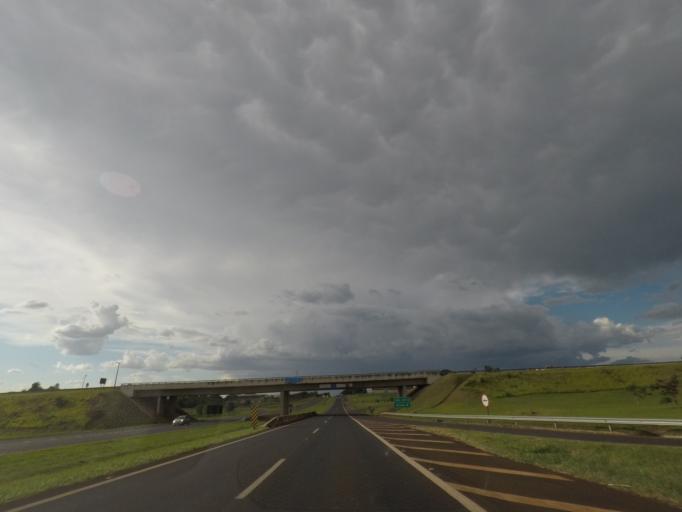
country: BR
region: Sao Paulo
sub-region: Jardinopolis
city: Jardinopolis
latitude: -21.0508
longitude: -47.8249
